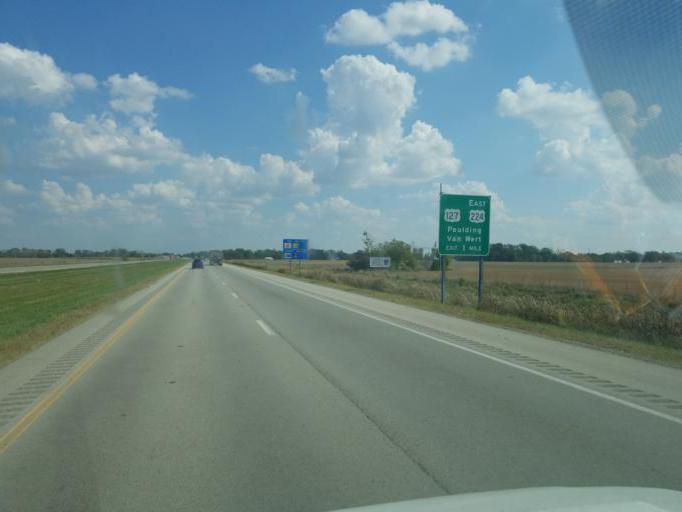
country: US
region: Ohio
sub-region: Van Wert County
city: Van Wert
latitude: 40.8887
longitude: -84.6017
